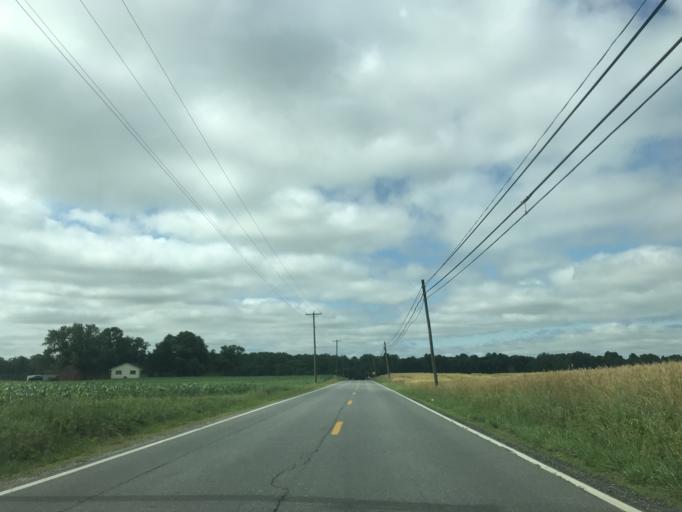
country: US
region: Maryland
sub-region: Caroline County
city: Ridgely
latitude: 38.8982
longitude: -75.9592
